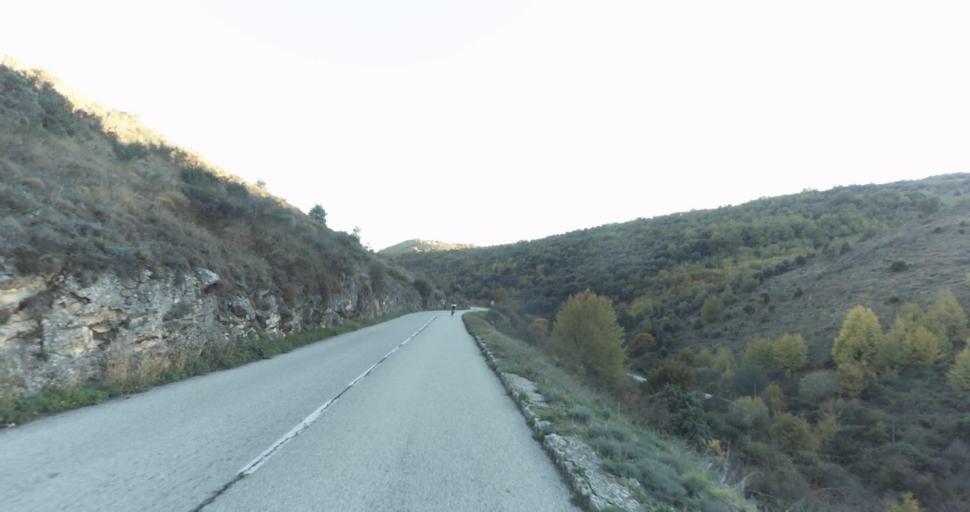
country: FR
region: Provence-Alpes-Cote d'Azur
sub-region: Departement des Alpes-Maritimes
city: Vence
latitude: 43.7510
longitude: 7.0959
